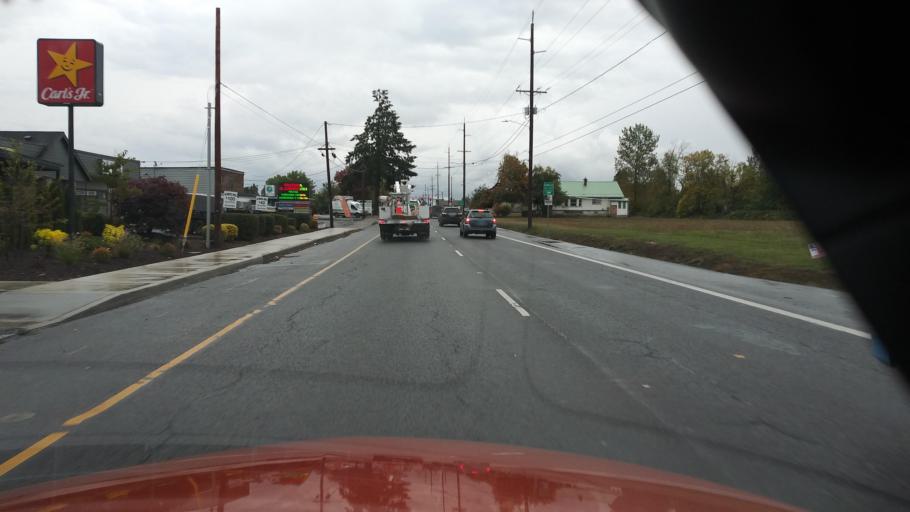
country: US
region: Oregon
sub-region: Washington County
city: Cornelius
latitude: 45.5201
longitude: -123.0704
